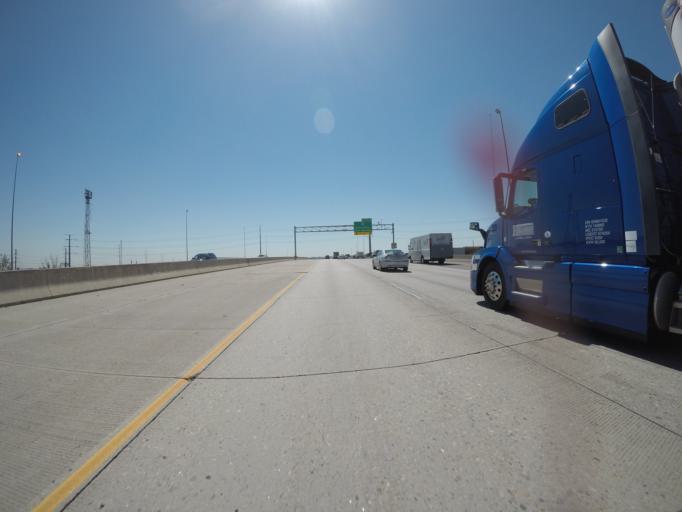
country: US
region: Colorado
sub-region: Adams County
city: Berkley
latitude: 39.7827
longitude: -104.9994
